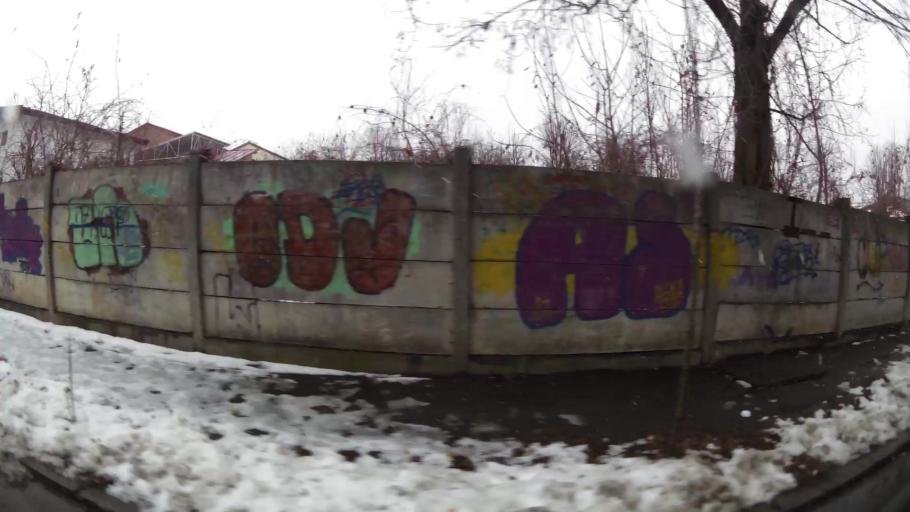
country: RO
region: Ilfov
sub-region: Comuna Chiajna
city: Rosu
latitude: 44.4916
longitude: 26.0436
